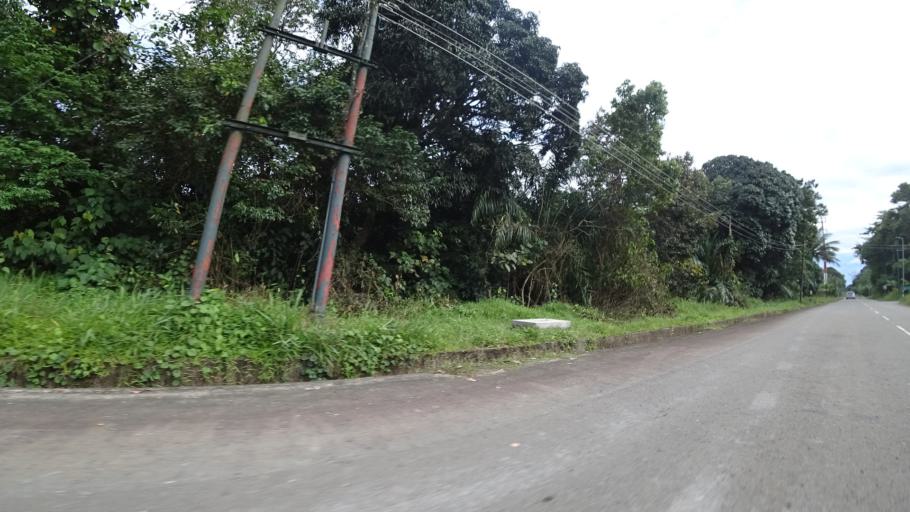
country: MY
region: Sarawak
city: Limbang
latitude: 4.8302
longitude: 114.9485
